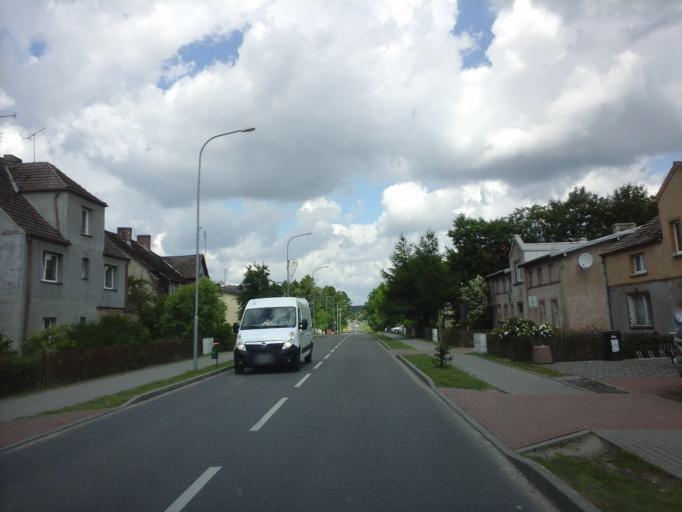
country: PL
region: West Pomeranian Voivodeship
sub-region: Powiat swidwinski
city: Slawoborze
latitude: 53.8924
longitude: 15.7109
